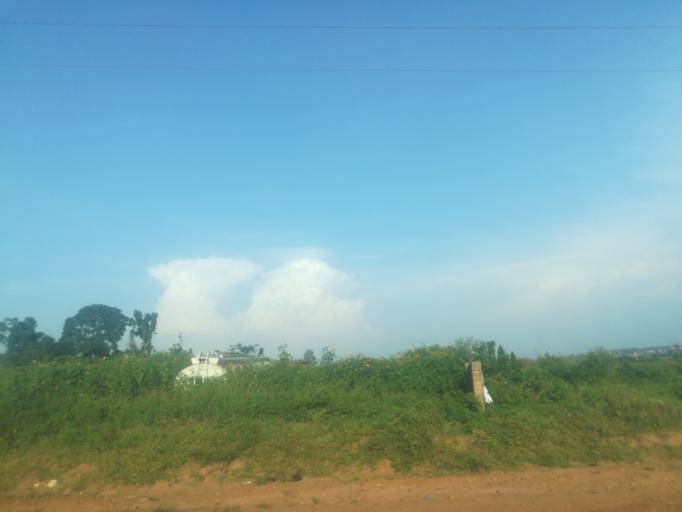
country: NG
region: Oyo
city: Moniya
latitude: 7.5585
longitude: 3.8878
